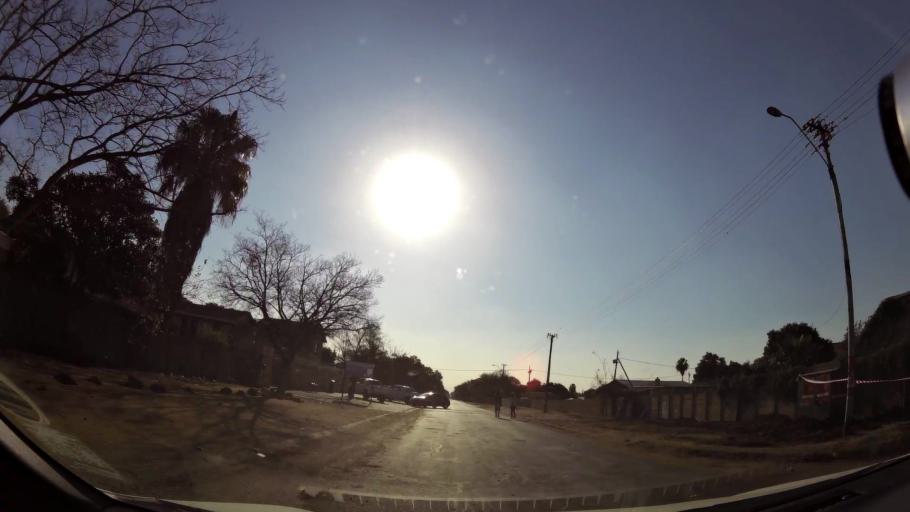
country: ZA
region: North-West
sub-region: Bojanala Platinum District Municipality
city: Rustenburg
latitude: -25.6596
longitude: 27.2599
